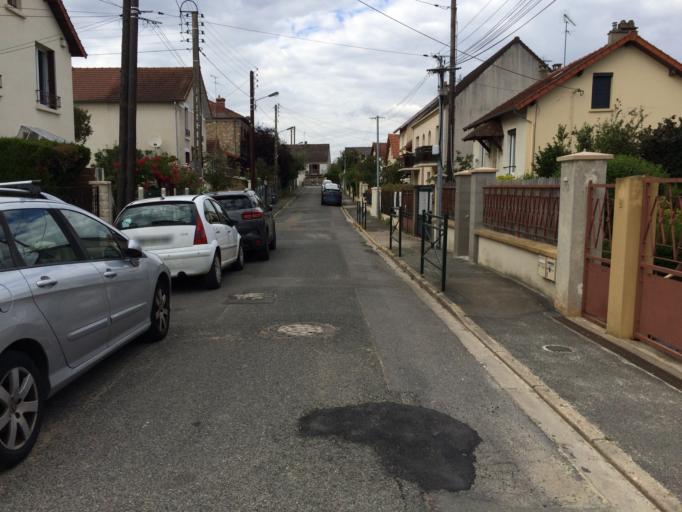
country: FR
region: Ile-de-France
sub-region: Departement de l'Essonne
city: Palaiseau
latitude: 48.7263
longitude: 2.2382
